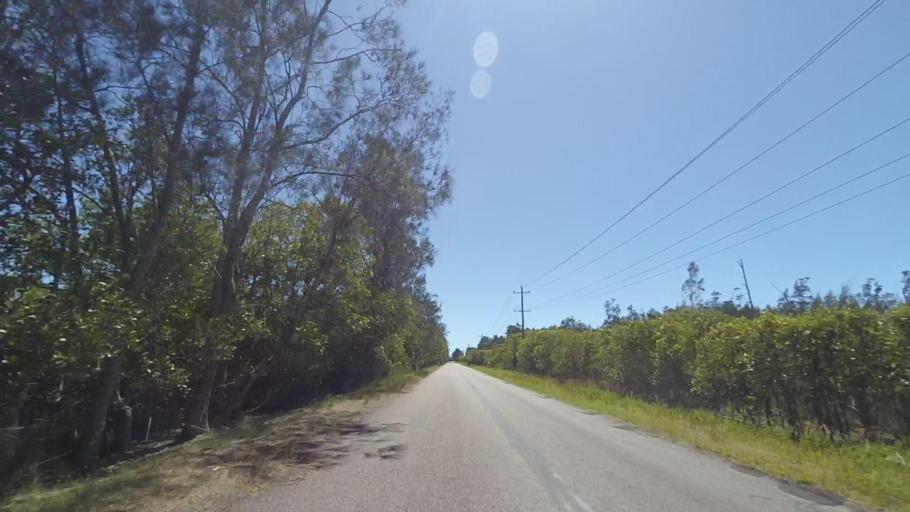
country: AU
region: New South Wales
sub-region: Port Stephens Shire
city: Medowie
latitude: -32.7858
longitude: 151.9374
